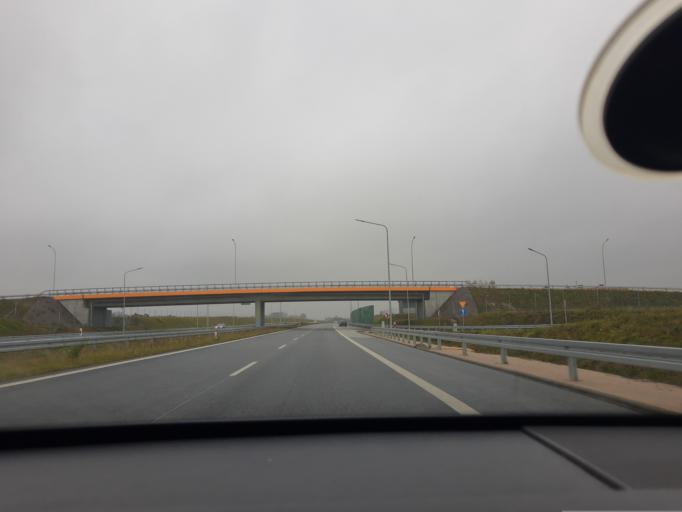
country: PL
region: Lodz Voivodeship
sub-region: Powiat pabianicki
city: Pabianice
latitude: 51.6999
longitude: 19.3420
